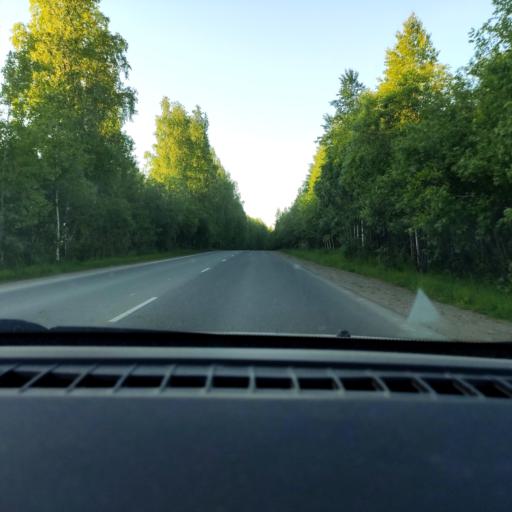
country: RU
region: Perm
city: Polazna
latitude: 58.1186
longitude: 56.4293
